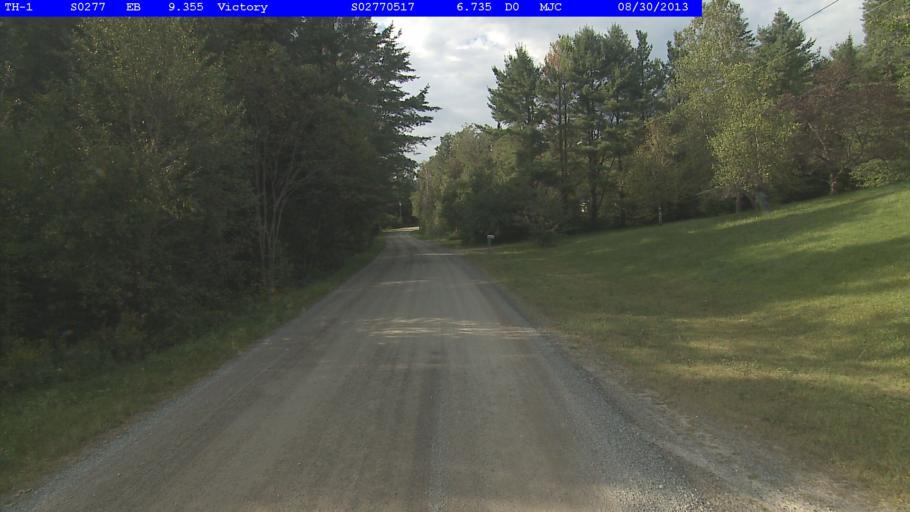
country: US
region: Vermont
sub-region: Caledonia County
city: Lyndonville
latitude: 44.5651
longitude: -71.7880
